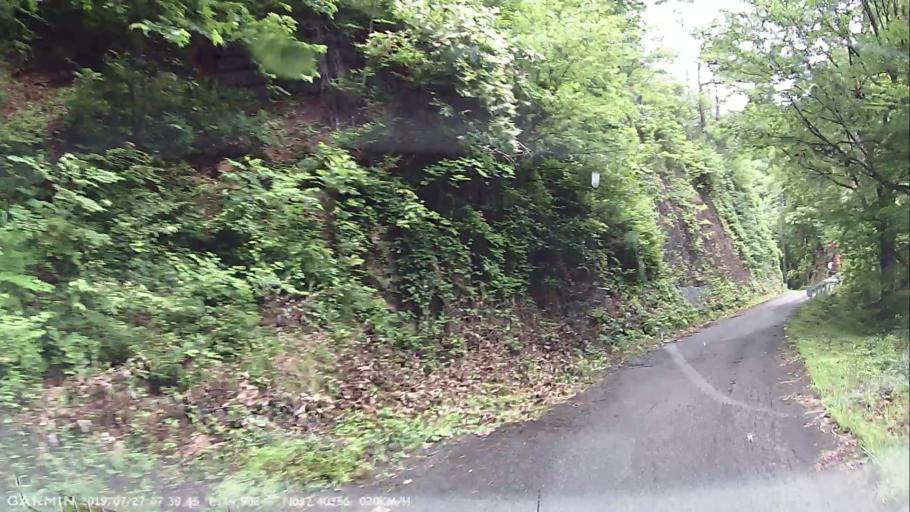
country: JP
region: Fukushima
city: Inawashiro
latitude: 37.4036
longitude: 139.9525
